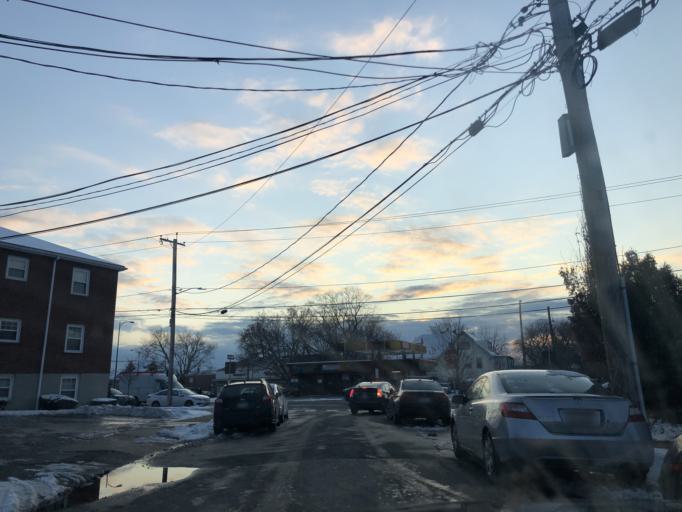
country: US
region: Massachusetts
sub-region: Middlesex County
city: Arlington
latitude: 42.4110
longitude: -71.1475
